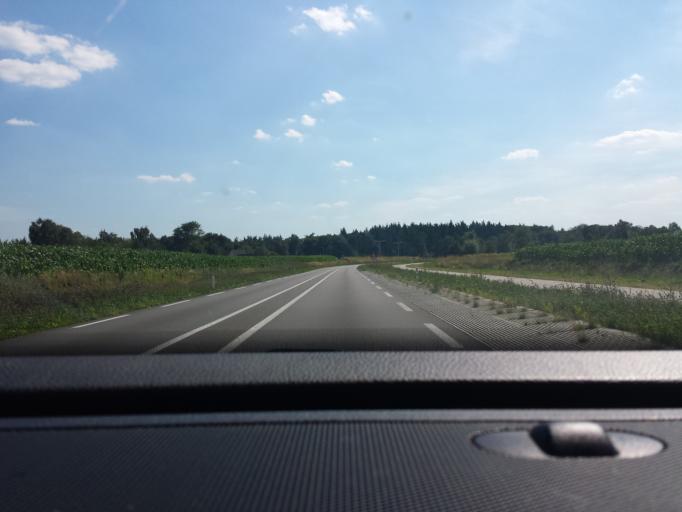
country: NL
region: Gelderland
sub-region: Gemeente Bronckhorst
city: Baak
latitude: 52.0068
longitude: 6.2294
